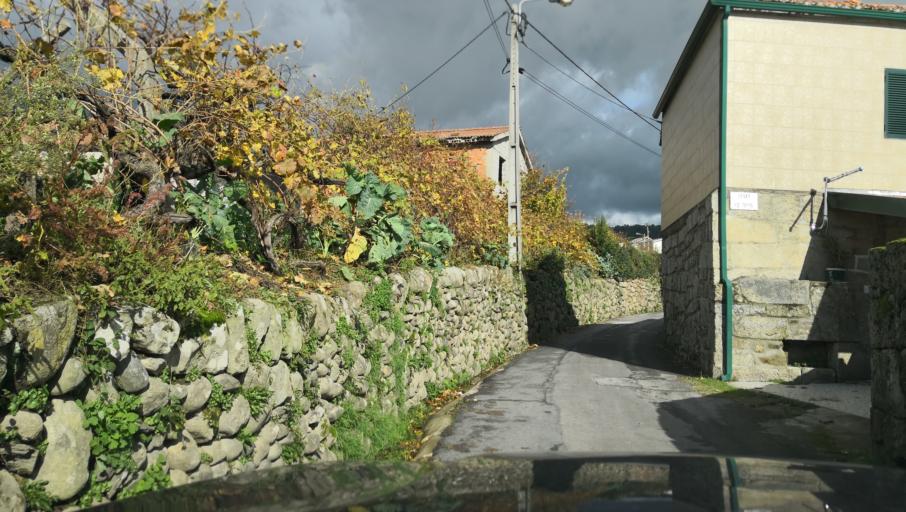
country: PT
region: Vila Real
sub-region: Vila Real
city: Vila Real
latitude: 41.3177
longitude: -7.7611
